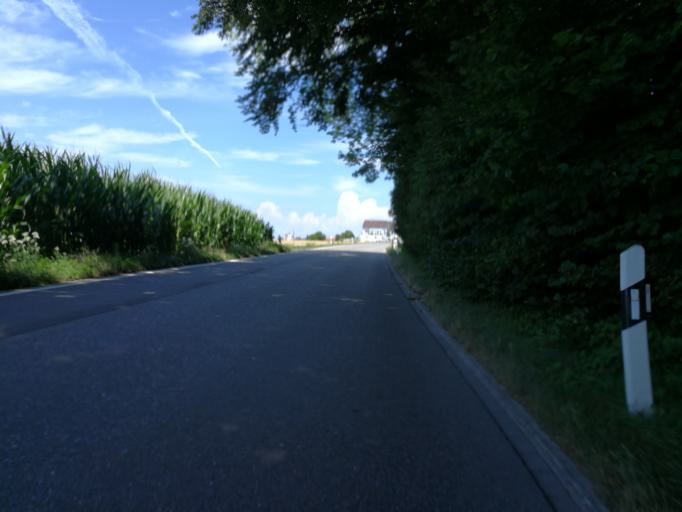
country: CH
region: Zurich
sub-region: Bezirk Hinwil
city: Wetzikon / Kempten
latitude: 47.3192
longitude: 8.8167
